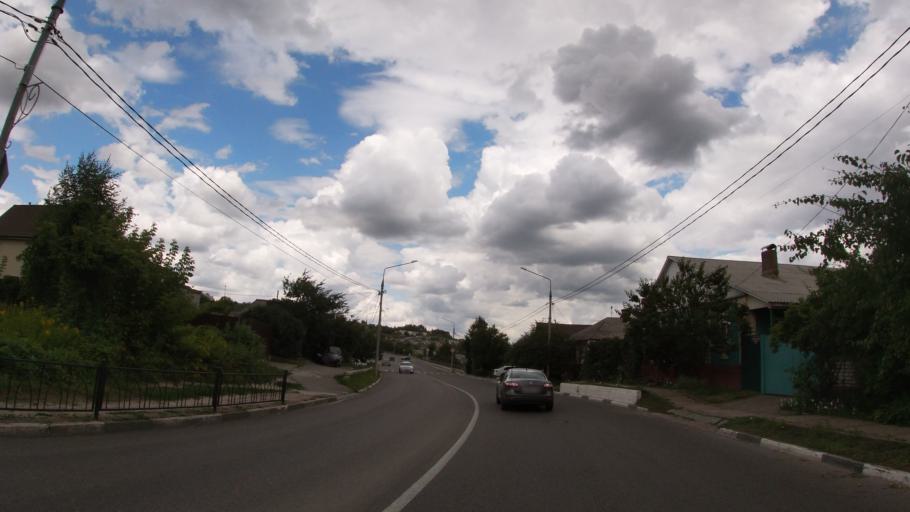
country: RU
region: Belgorod
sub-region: Belgorodskiy Rayon
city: Belgorod
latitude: 50.6069
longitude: 36.6126
